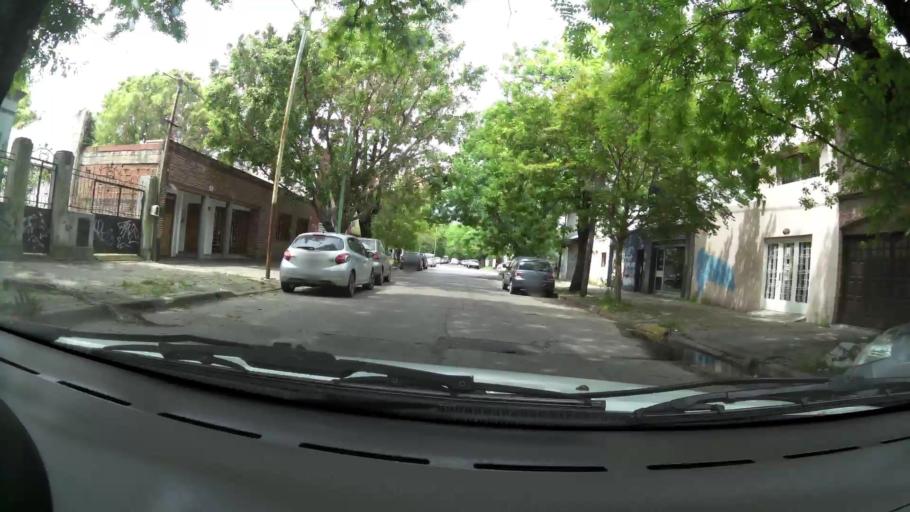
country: AR
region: Buenos Aires
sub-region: Partido de La Plata
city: La Plata
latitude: -34.9312
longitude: -57.9473
